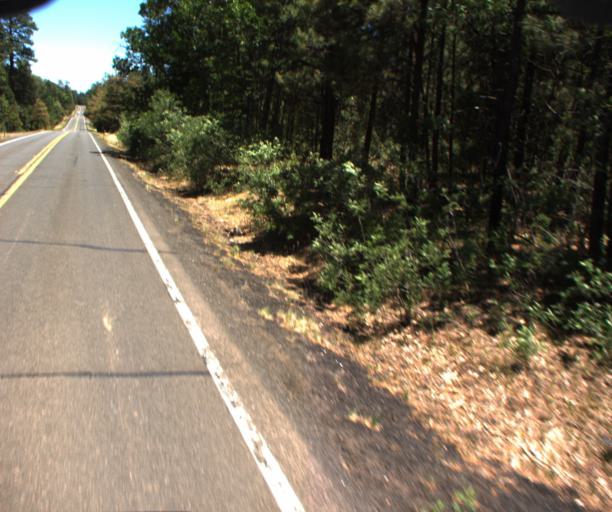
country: US
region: Arizona
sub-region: Gila County
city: Pine
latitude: 34.6075
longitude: -111.2070
